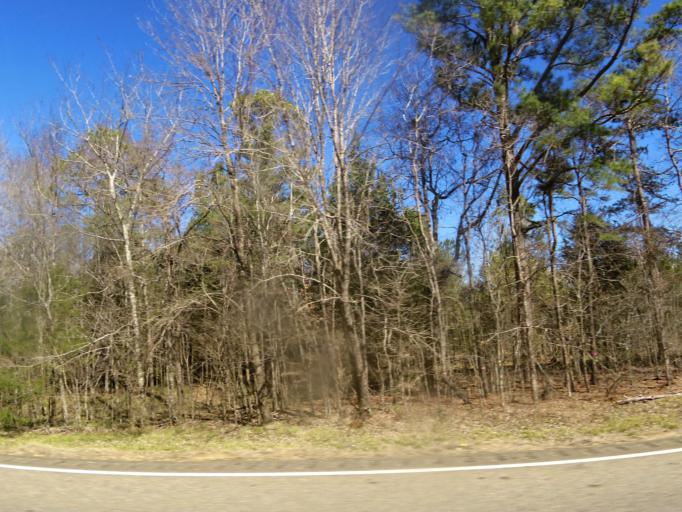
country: US
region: Alabama
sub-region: Montgomery County
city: Pike Road
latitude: 32.1762
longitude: -86.0793
